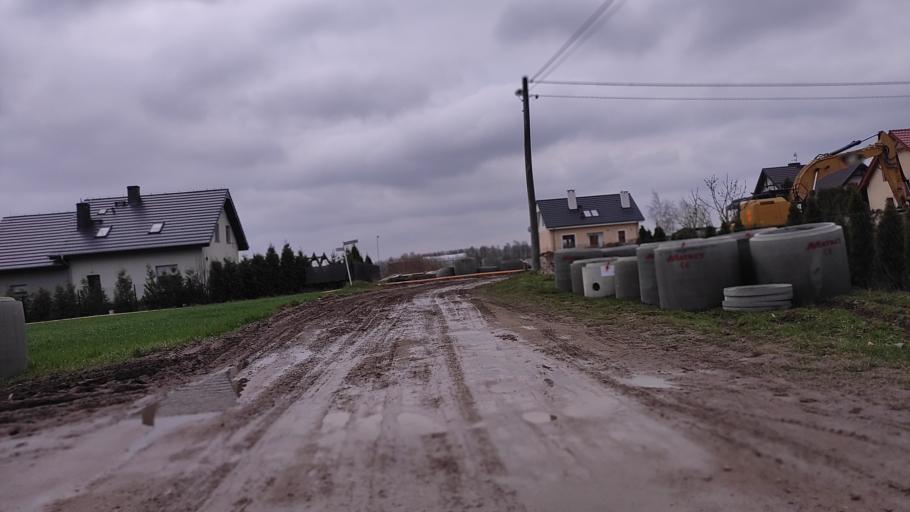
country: PL
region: Greater Poland Voivodeship
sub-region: Powiat poznanski
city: Kostrzyn
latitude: 52.4016
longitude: 17.1724
